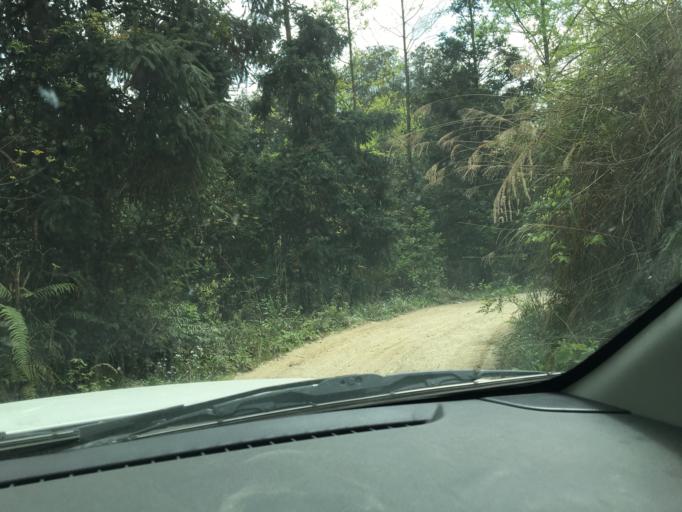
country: CN
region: Guizhou Sheng
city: Kuanping
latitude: 28.0252
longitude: 108.0537
